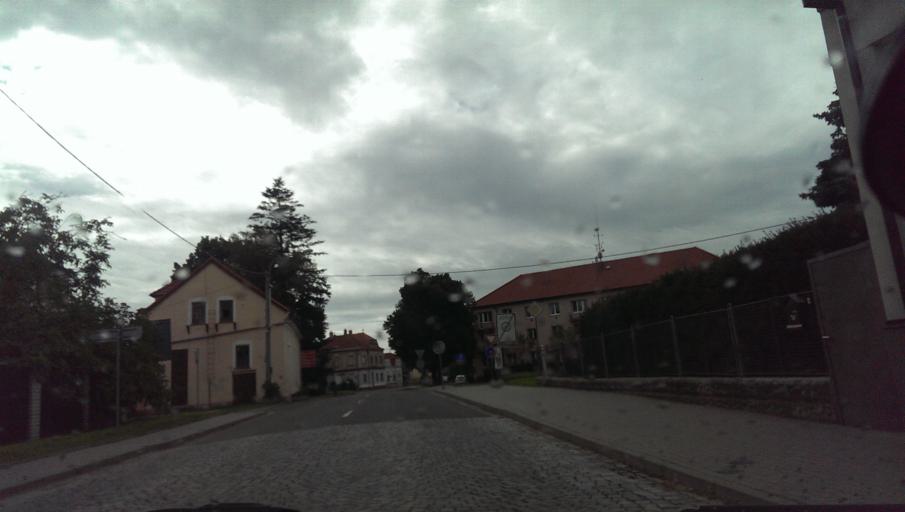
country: CZ
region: Zlin
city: Uhersky Ostroh
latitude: 48.9839
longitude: 17.3870
